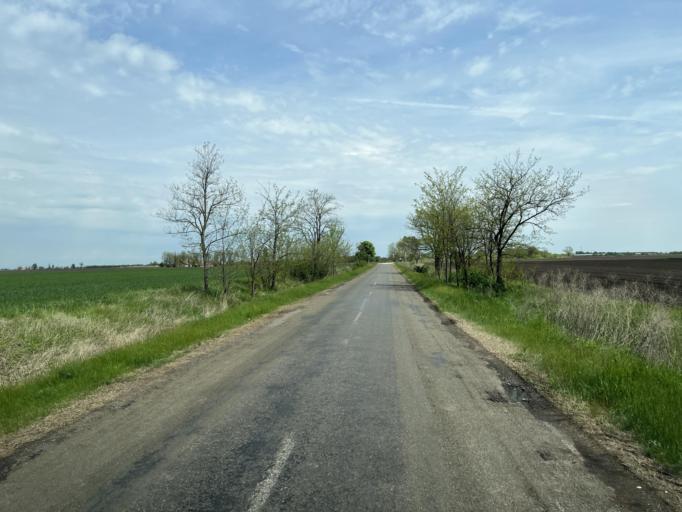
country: HU
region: Pest
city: Tapiogyorgye
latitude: 47.3572
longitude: 19.9722
